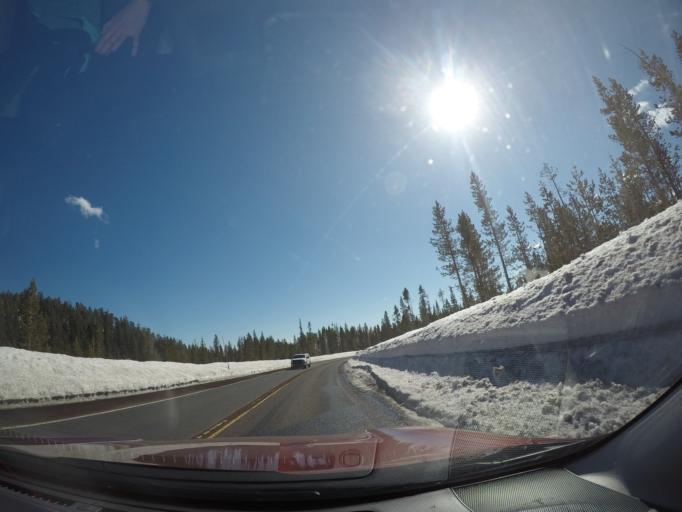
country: US
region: Oregon
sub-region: Deschutes County
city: Sunriver
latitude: 43.9769
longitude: -121.6103
